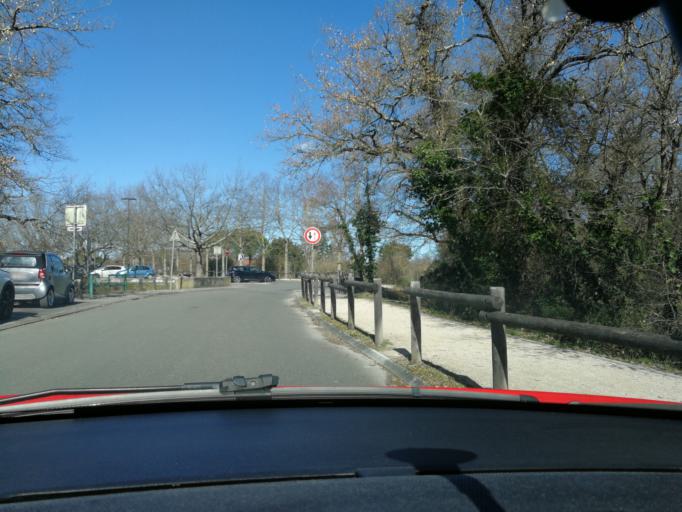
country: FR
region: Midi-Pyrenees
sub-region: Departement de la Haute-Garonne
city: Cugnaux
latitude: 43.5628
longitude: 1.3480
